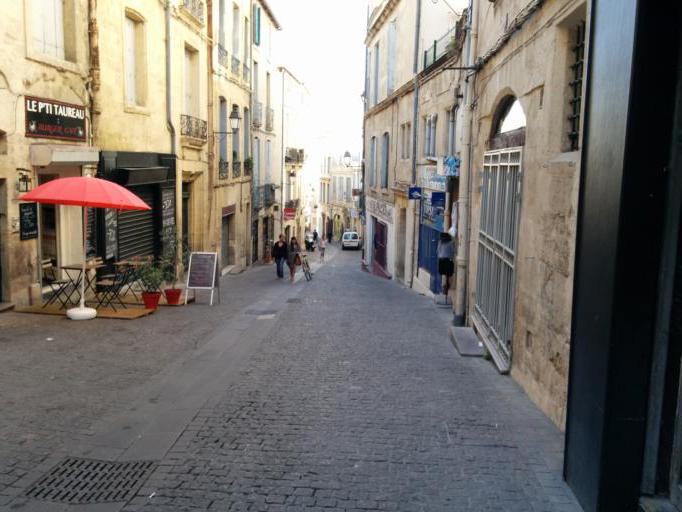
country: FR
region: Languedoc-Roussillon
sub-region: Departement de l'Herault
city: Montpellier
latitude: 43.6120
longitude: 3.8764
